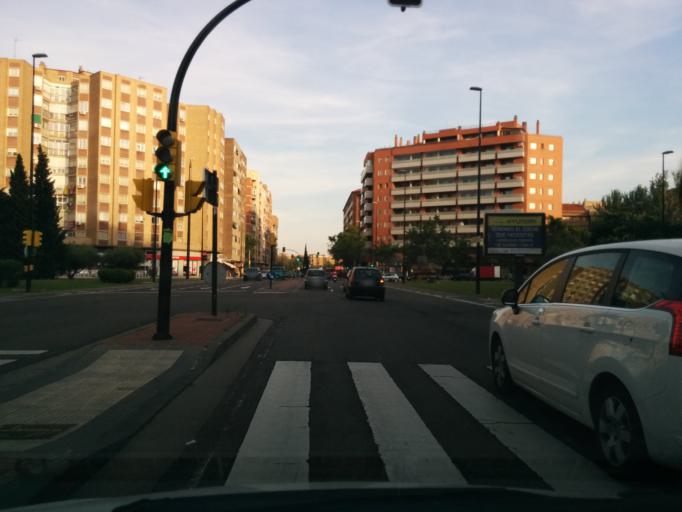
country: ES
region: Aragon
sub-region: Provincia de Zaragoza
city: Zaragoza
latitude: 41.6627
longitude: -0.8655
